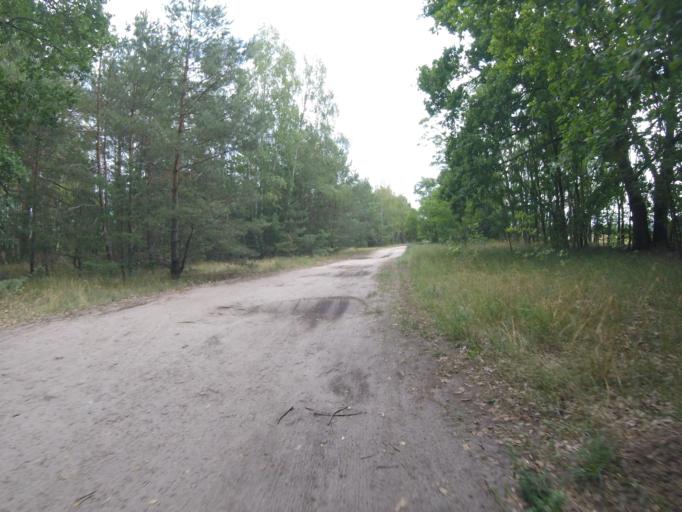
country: DE
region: Brandenburg
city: Halbe
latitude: 52.1470
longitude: 13.6931
